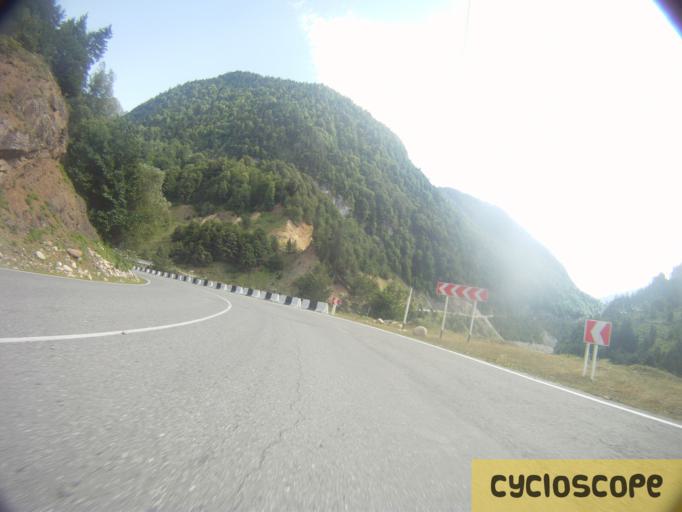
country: GE
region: Samegrelo and Zemo Svaneti
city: Jvari
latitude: 42.9310
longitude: 42.1122
